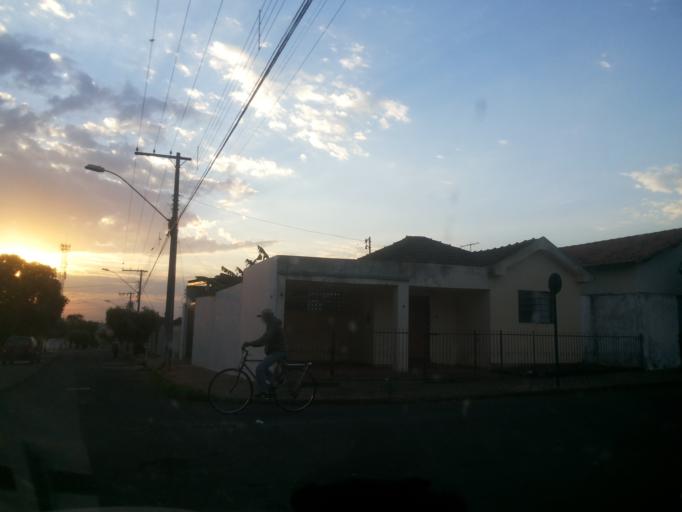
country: BR
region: Minas Gerais
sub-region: Ituiutaba
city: Ituiutaba
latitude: -18.9805
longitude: -49.4552
